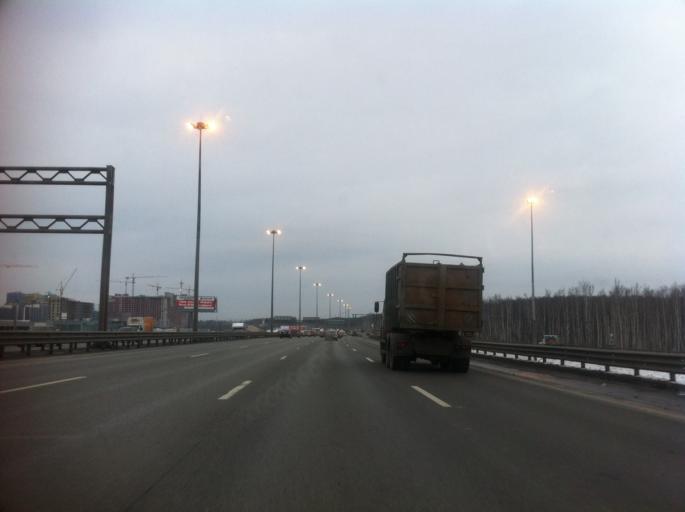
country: RU
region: Leningrad
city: Rybatskoye
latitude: 59.8857
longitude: 30.5257
